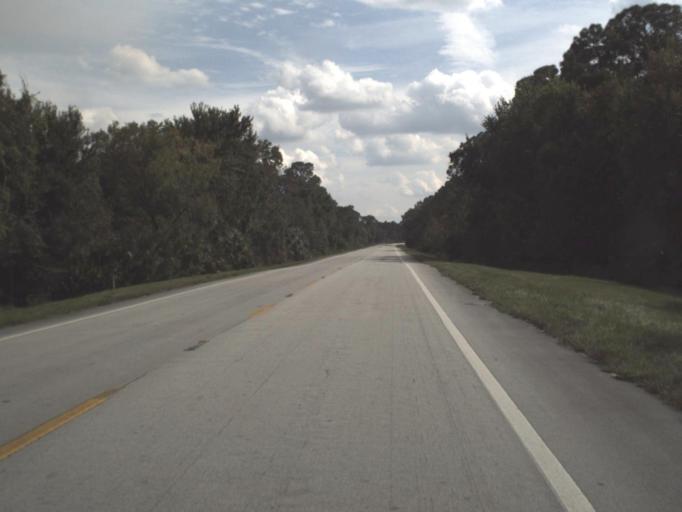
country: US
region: Florida
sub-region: Indian River County
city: Fellsmere
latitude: 27.5853
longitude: -80.8385
